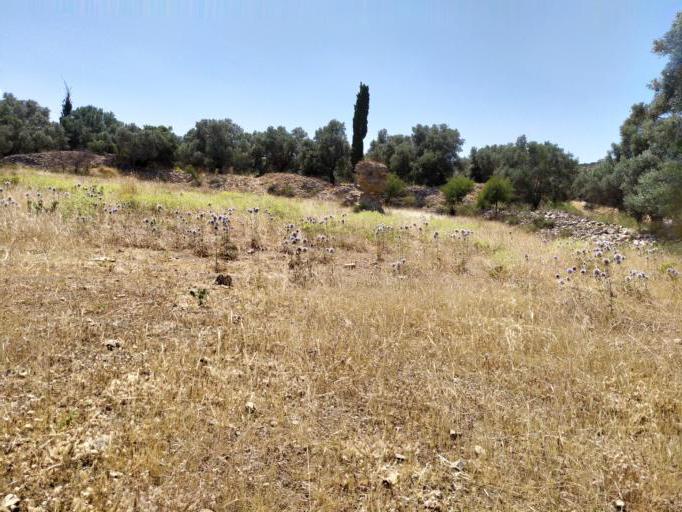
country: GR
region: Crete
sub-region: Nomos Irakleiou
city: Agioi Deka
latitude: 35.0605
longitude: 24.9501
